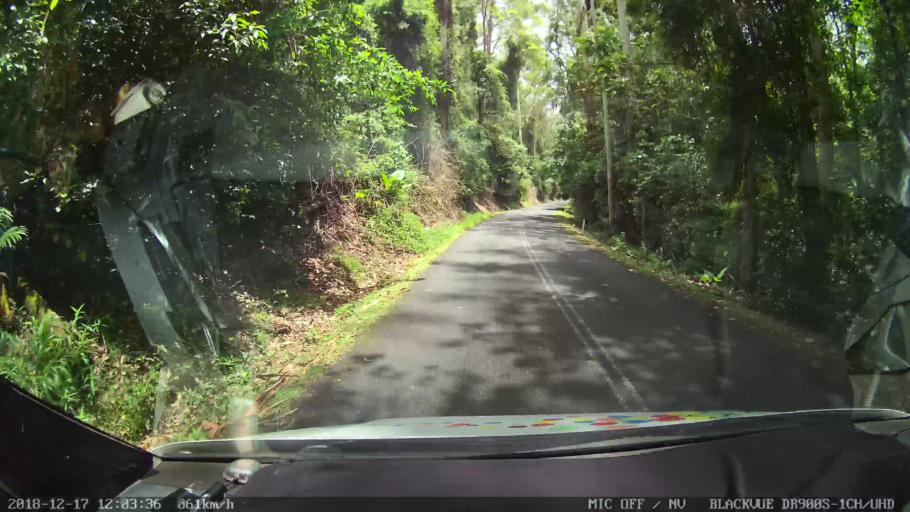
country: AU
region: New South Wales
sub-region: Kyogle
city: Kyogle
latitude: -28.5067
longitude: 152.5678
